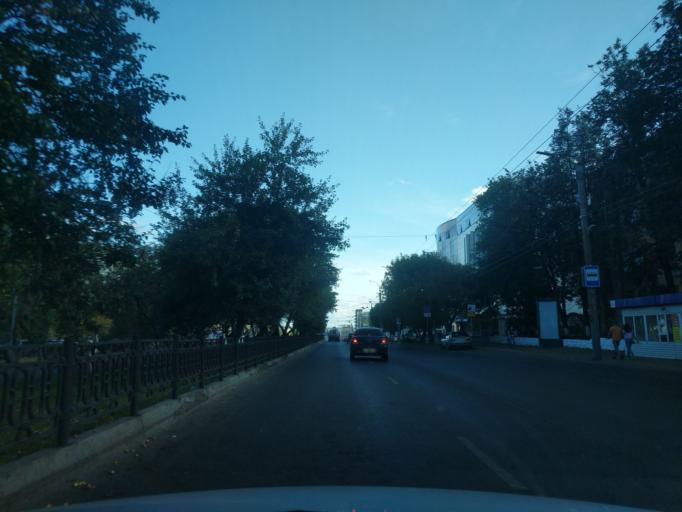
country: RU
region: Kirov
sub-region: Kirovo-Chepetskiy Rayon
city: Kirov
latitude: 58.5952
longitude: 49.6578
